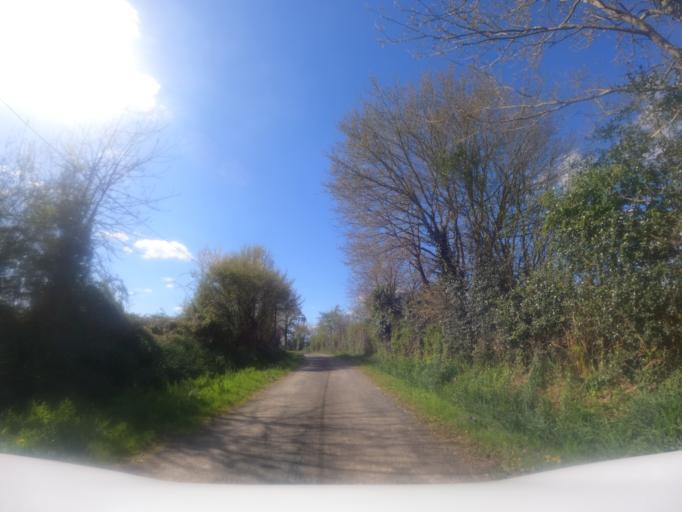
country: FR
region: Pays de la Loire
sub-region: Departement de la Vendee
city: Saint-Vincent-sur-Graon
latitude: 46.5292
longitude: -1.3775
